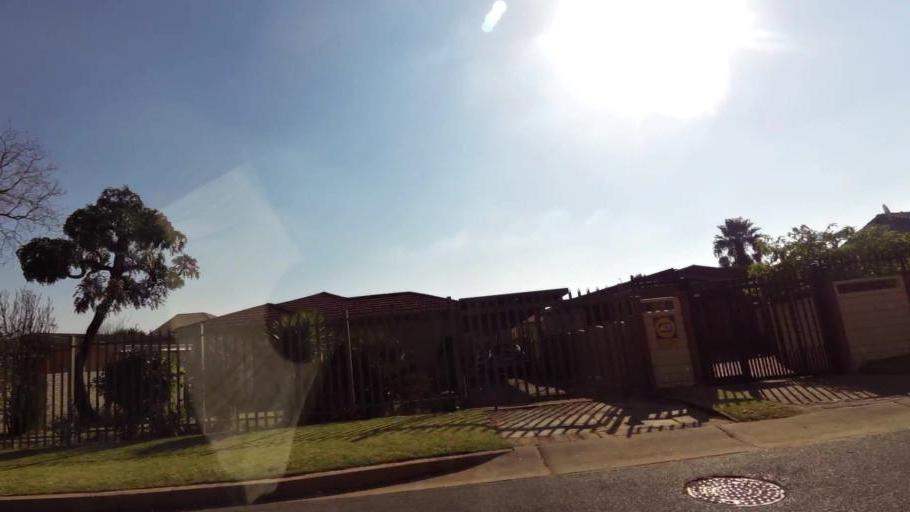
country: ZA
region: Gauteng
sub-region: City of Johannesburg Metropolitan Municipality
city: Johannesburg
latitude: -26.1720
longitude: 27.9792
